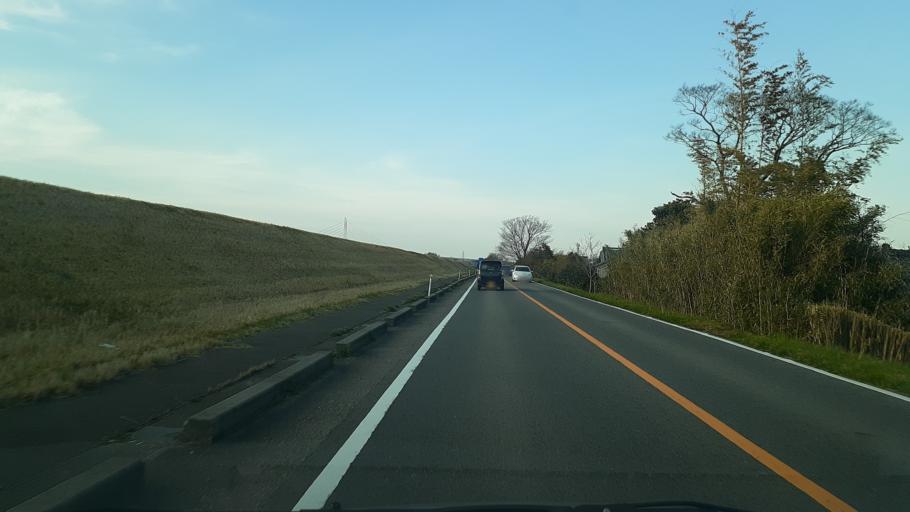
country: JP
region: Niigata
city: Niigata-shi
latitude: 37.8616
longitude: 139.0252
